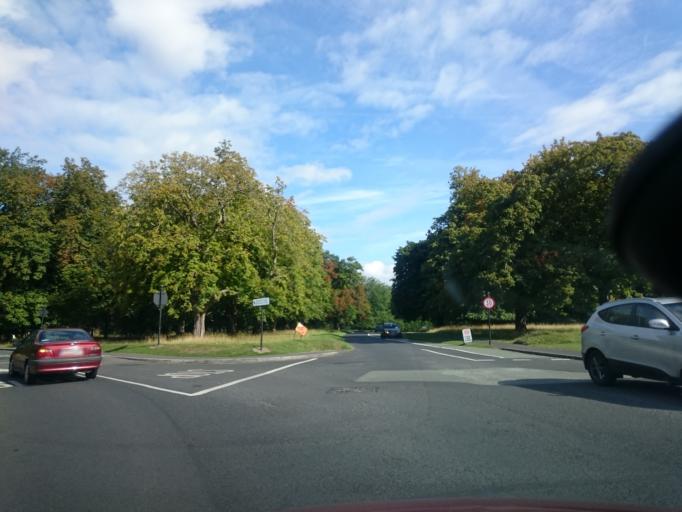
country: IE
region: Leinster
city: Chapelizod
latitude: 53.3605
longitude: -6.3258
